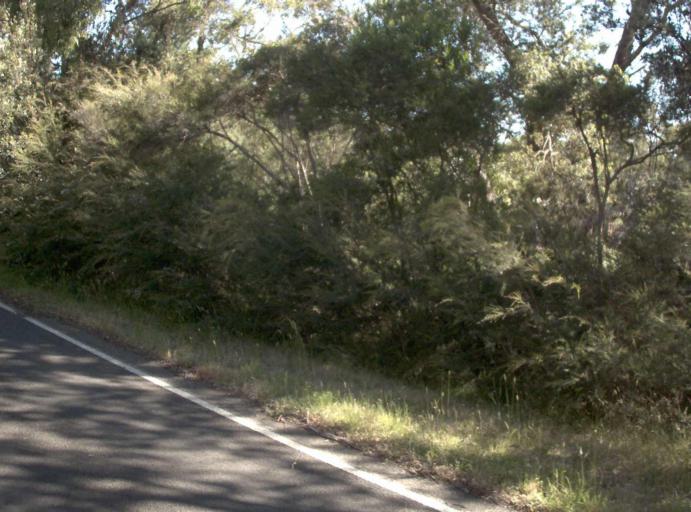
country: AU
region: Victoria
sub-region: Latrobe
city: Traralgon
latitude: -38.6597
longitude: 146.6826
